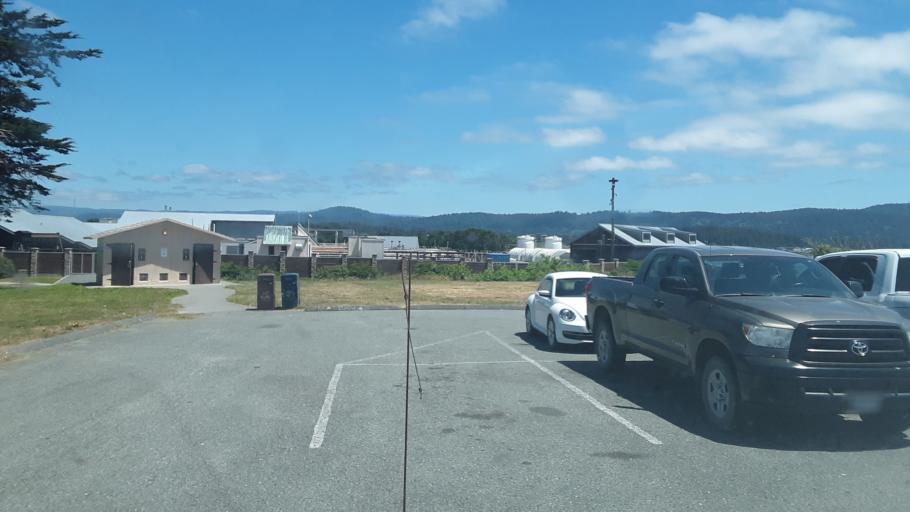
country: US
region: California
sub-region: Del Norte County
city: Crescent City
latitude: 41.7464
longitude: -124.2018
